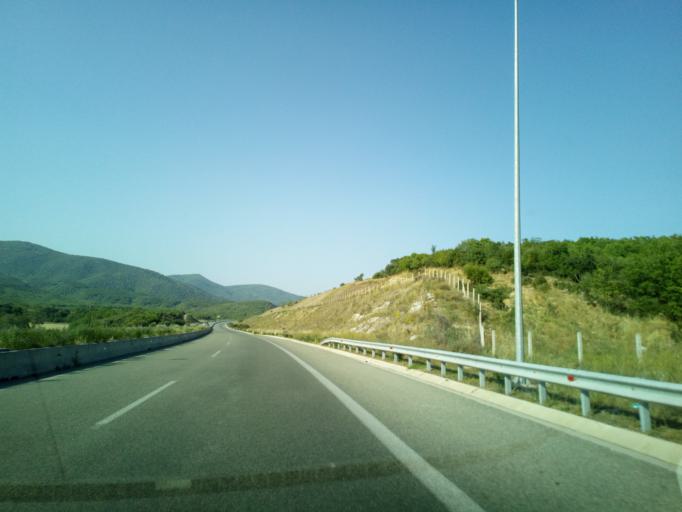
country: GR
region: Central Macedonia
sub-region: Nomos Thessalonikis
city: Stavros
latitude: 40.6822
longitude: 23.6192
